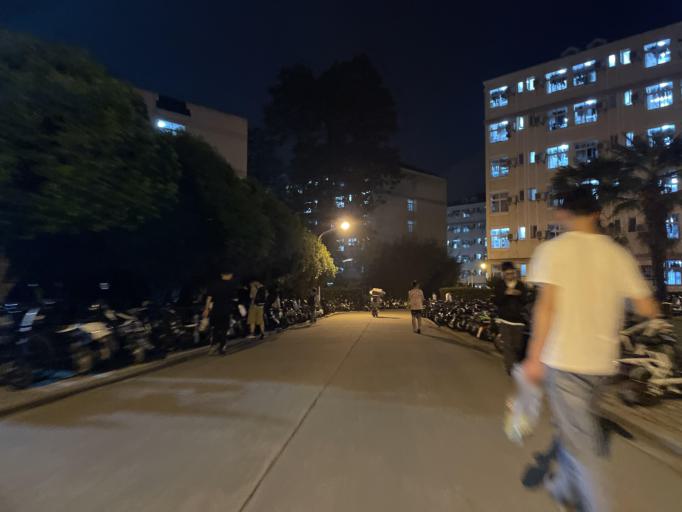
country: CN
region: Hubei
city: Guanshan
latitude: 30.5176
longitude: 114.4285
